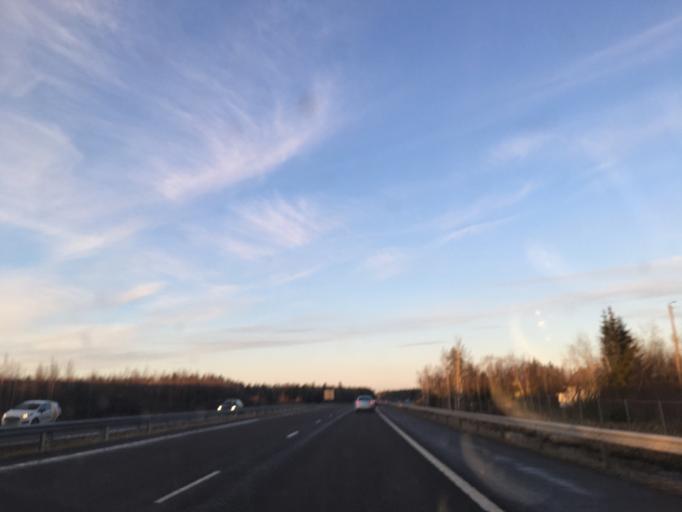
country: FI
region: Varsinais-Suomi
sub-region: Turku
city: Turku
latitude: 60.5151
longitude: 22.3025
